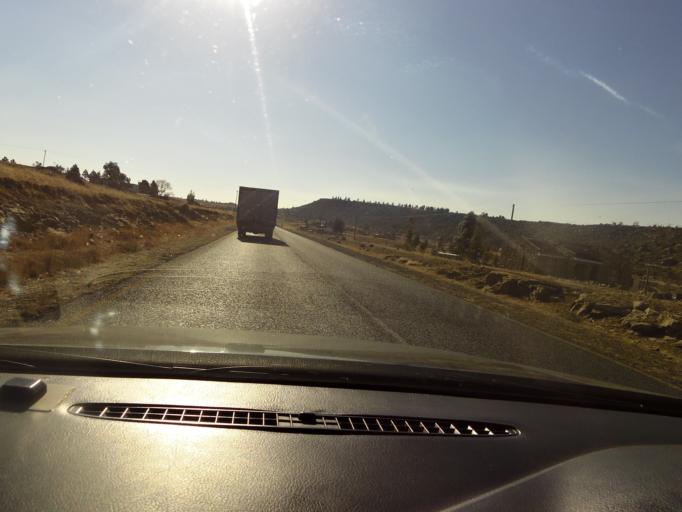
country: LS
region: Mohale's Hoek District
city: Mohale's Hoek
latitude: -30.0502
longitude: 27.4026
